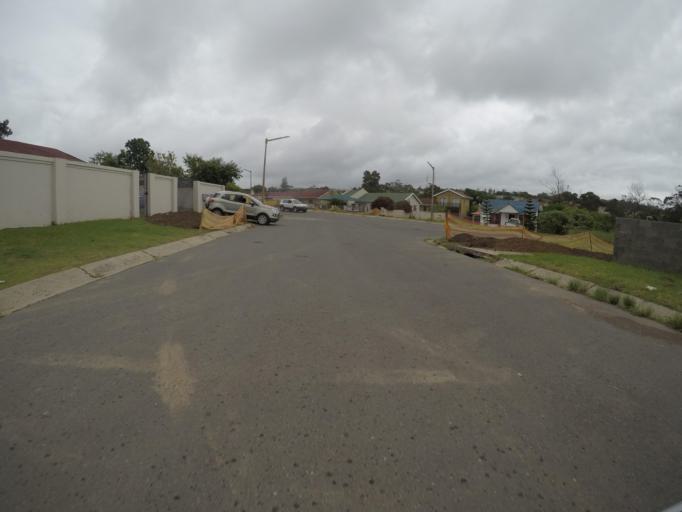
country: ZA
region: Eastern Cape
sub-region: Buffalo City Metropolitan Municipality
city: East London
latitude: -32.9940
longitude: 27.8388
